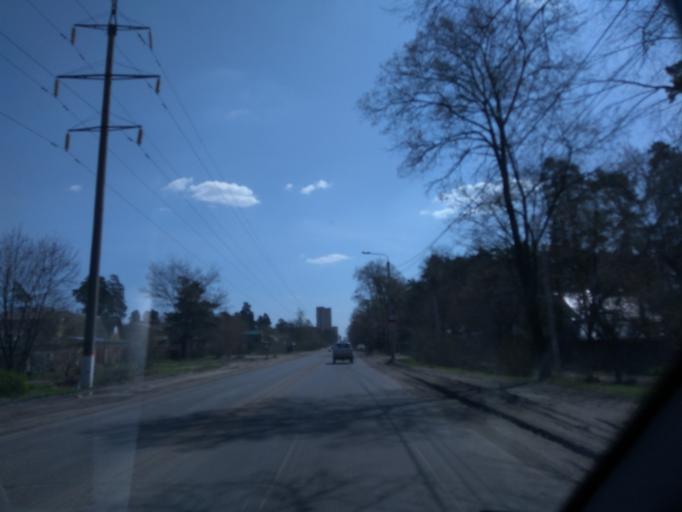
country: RU
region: Moskovskaya
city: Kratovo
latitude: 55.5718
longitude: 38.1856
